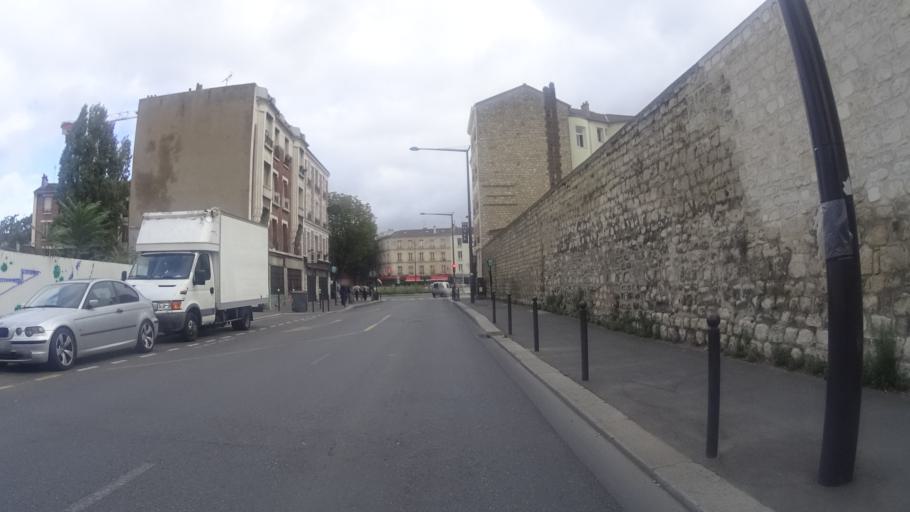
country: FR
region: Ile-de-France
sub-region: Departement du Val-de-Marne
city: Charenton-le-Pont
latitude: 48.8137
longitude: 2.4024
